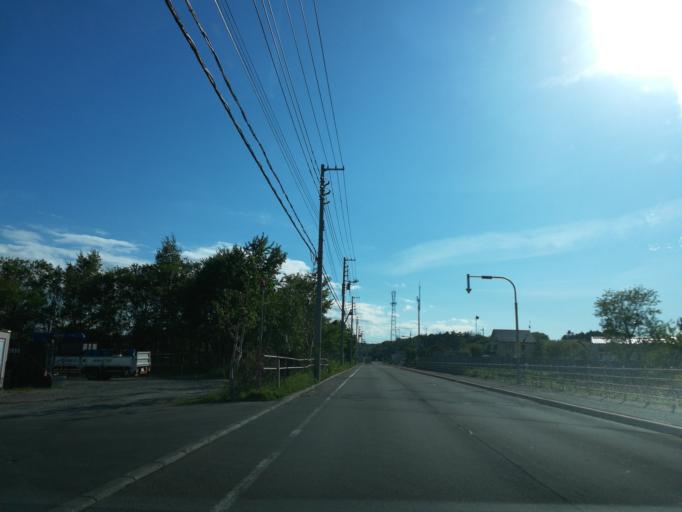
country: JP
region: Hokkaido
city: Kitahiroshima
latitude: 43.0104
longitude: 141.5621
